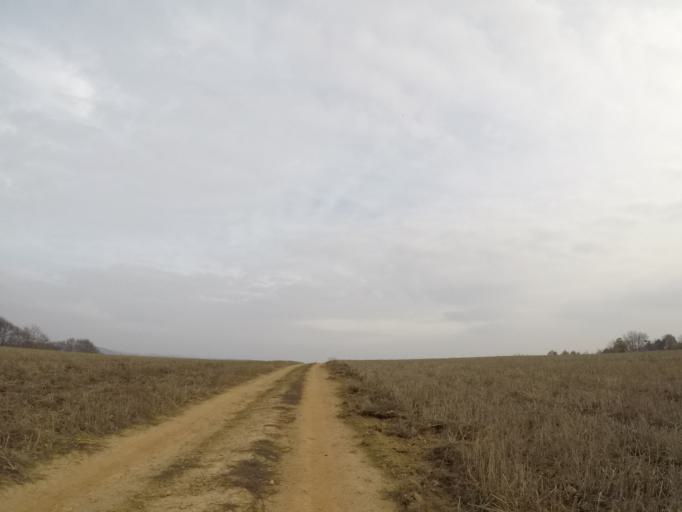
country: SK
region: Presovsky
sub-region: Okres Presov
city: Presov
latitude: 48.9404
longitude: 21.1512
